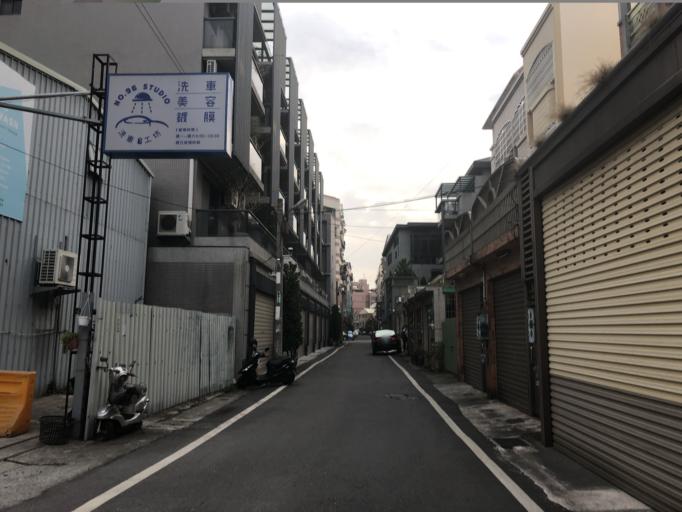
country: TW
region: Taiwan
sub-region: Changhua
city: Chang-hua
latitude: 23.9671
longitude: 120.5650
